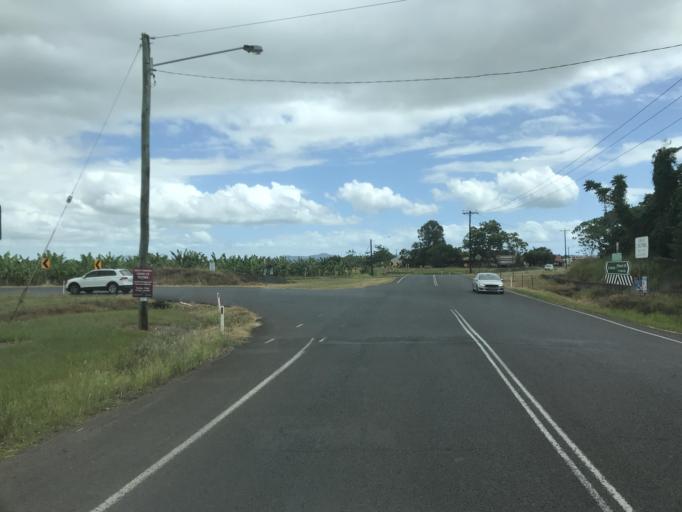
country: AU
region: Queensland
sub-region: Cassowary Coast
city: Innisfail
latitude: -17.5800
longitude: 146.0042
